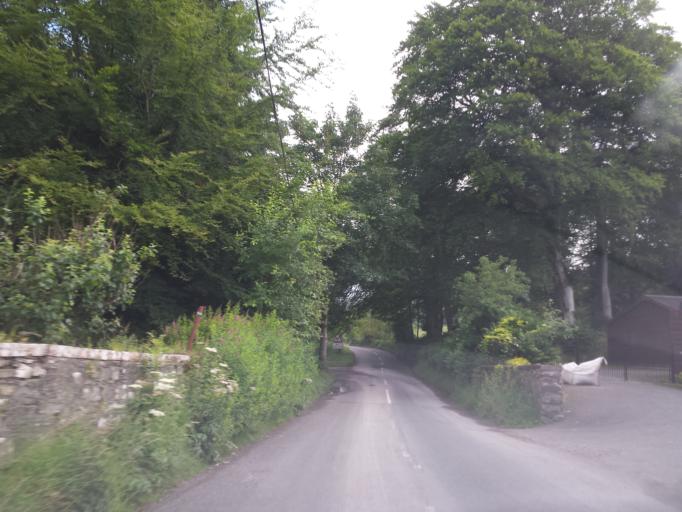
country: GB
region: Scotland
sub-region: Dumfries and Galloway
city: Moffat
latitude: 55.3391
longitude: -3.3841
